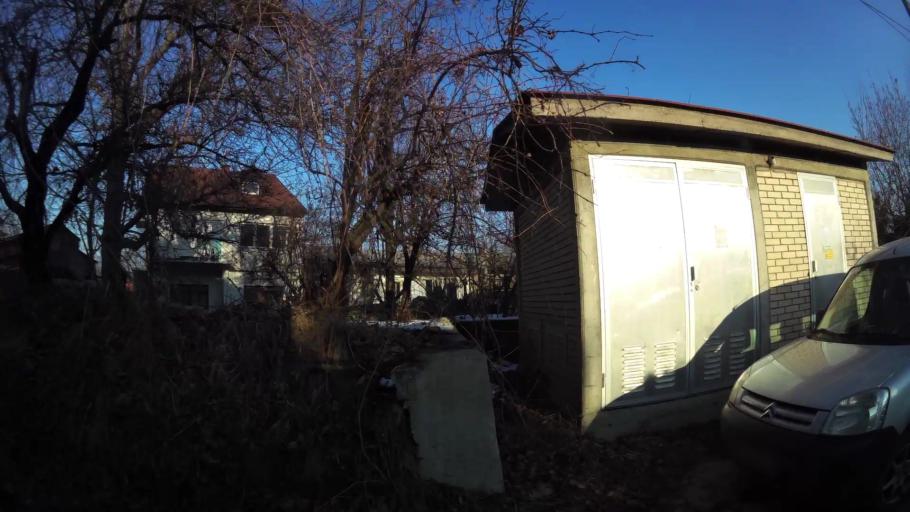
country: MK
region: Kisela Voda
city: Usje
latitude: 41.9705
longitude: 21.4741
